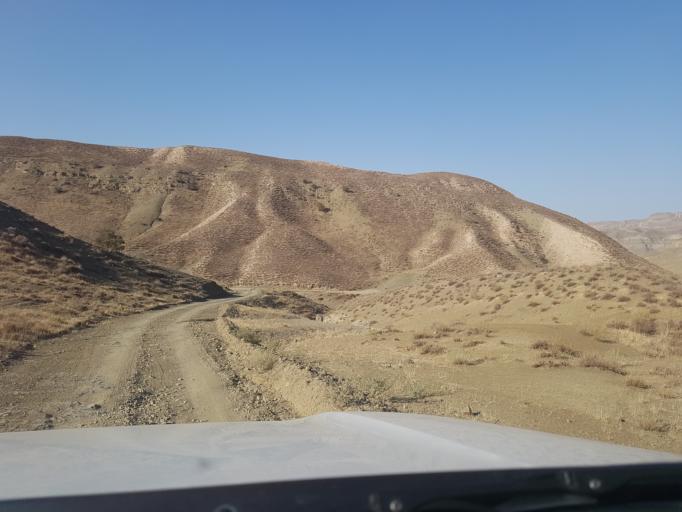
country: TM
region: Balkan
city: Magtymguly
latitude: 38.3020
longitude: 56.7773
